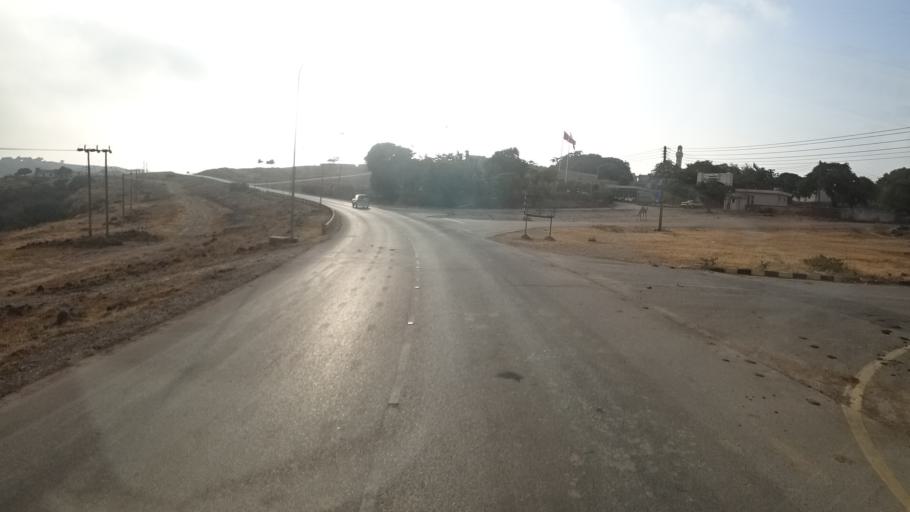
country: OM
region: Zufar
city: Salalah
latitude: 17.1255
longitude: 53.9966
